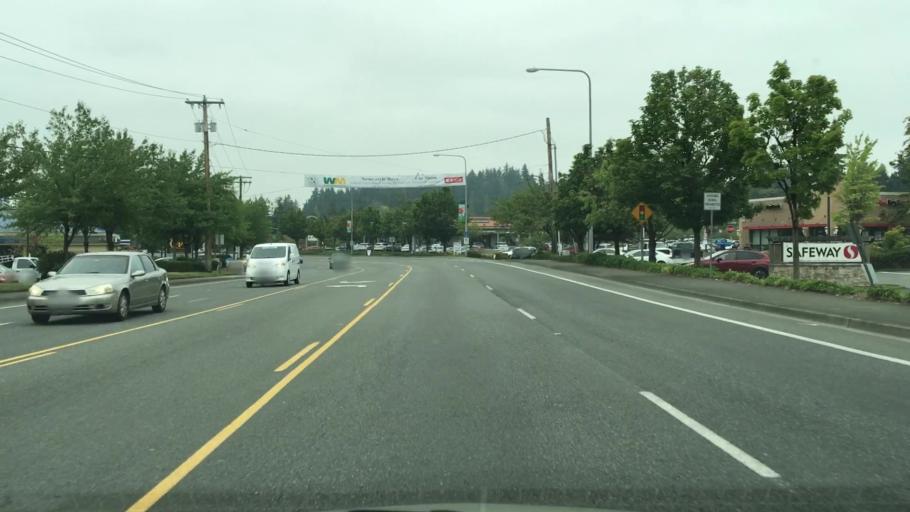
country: US
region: Washington
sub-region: King County
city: Newcastle
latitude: 47.5396
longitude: -122.1658
